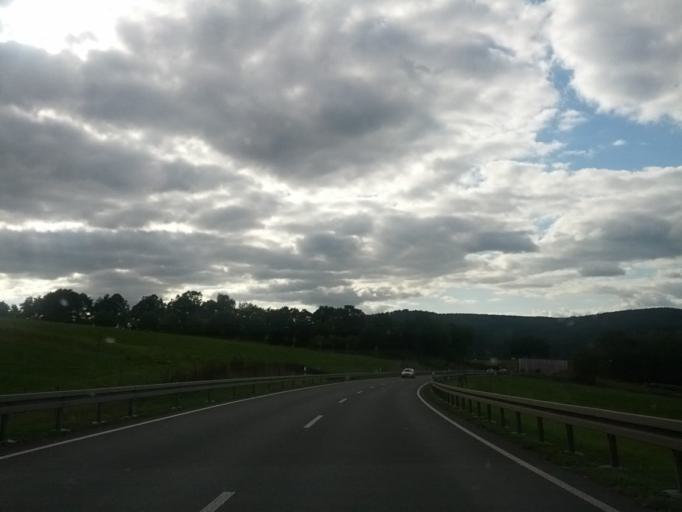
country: DE
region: Thuringia
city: Fambach
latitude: 50.7117
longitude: 10.3761
